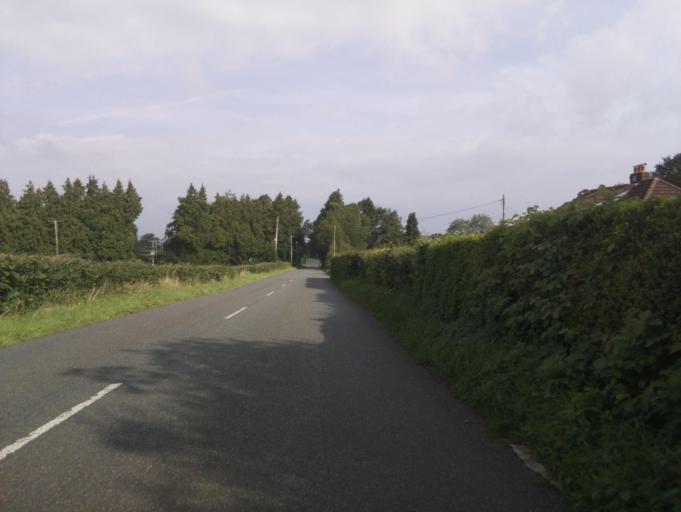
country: GB
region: England
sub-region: Bath and North East Somerset
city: East Harptree
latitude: 51.2963
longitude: -2.6002
